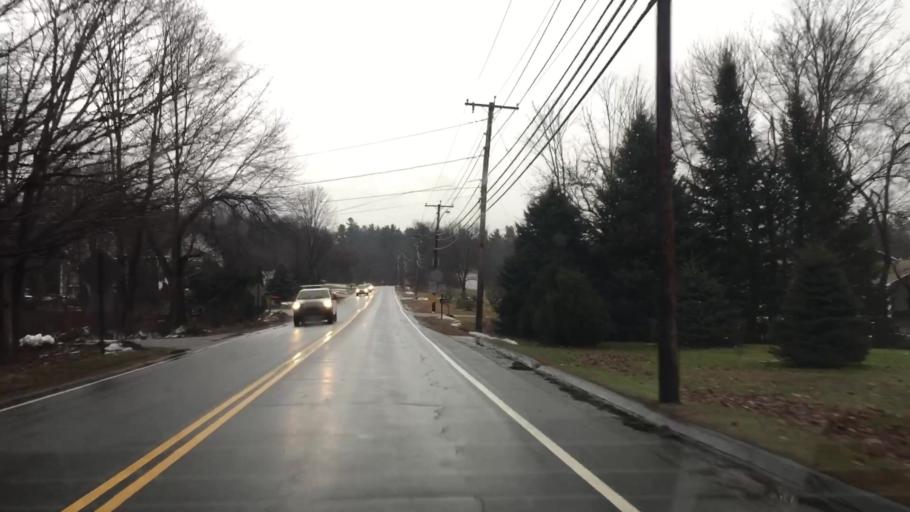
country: US
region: New Hampshire
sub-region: Hillsborough County
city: Pelham
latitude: 42.7096
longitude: -71.3435
